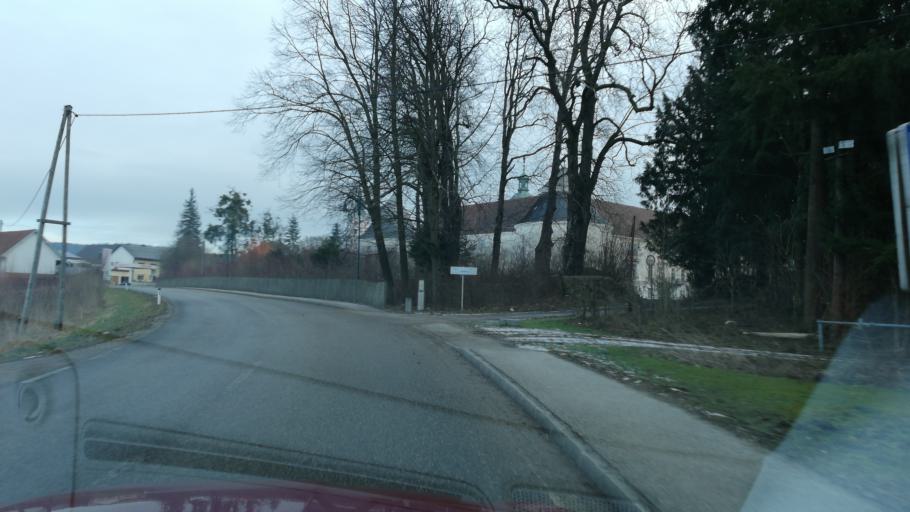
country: AT
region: Upper Austria
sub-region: Politischer Bezirk Vocklabruck
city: Niederthalheim
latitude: 48.1865
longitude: 13.7381
